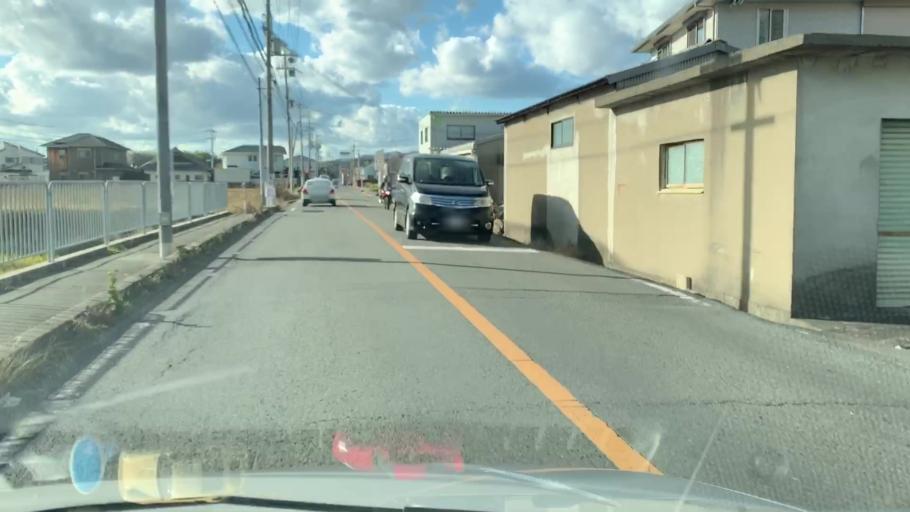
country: JP
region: Wakayama
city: Iwade
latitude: 34.2717
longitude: 135.2642
